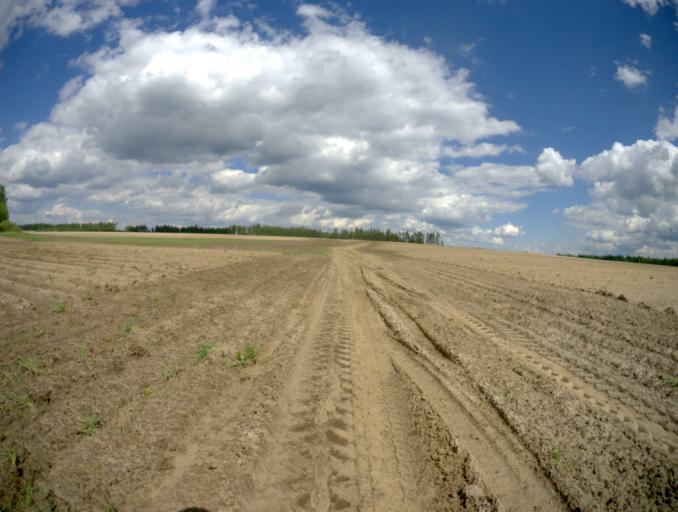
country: RU
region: Vladimir
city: Velikodvorskiy
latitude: 55.2724
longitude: 40.8380
